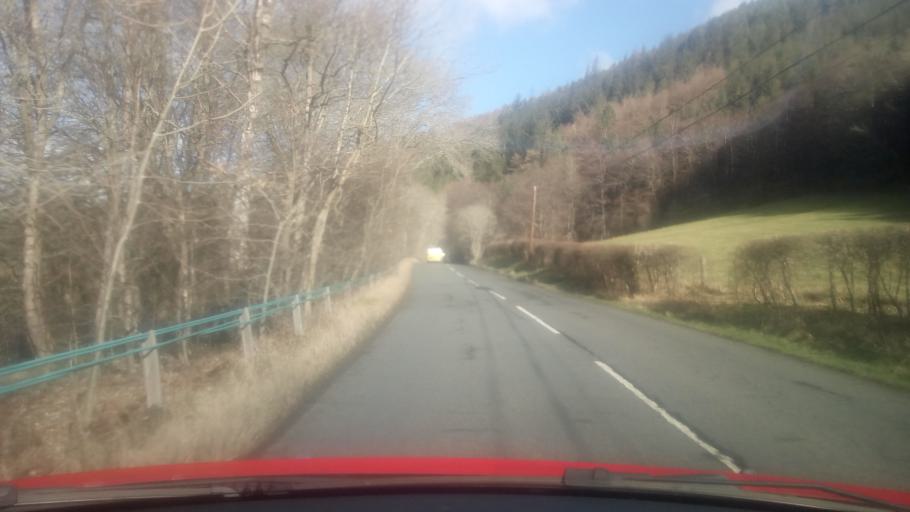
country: GB
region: Scotland
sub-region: The Scottish Borders
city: Selkirk
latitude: 55.5960
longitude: -2.8657
